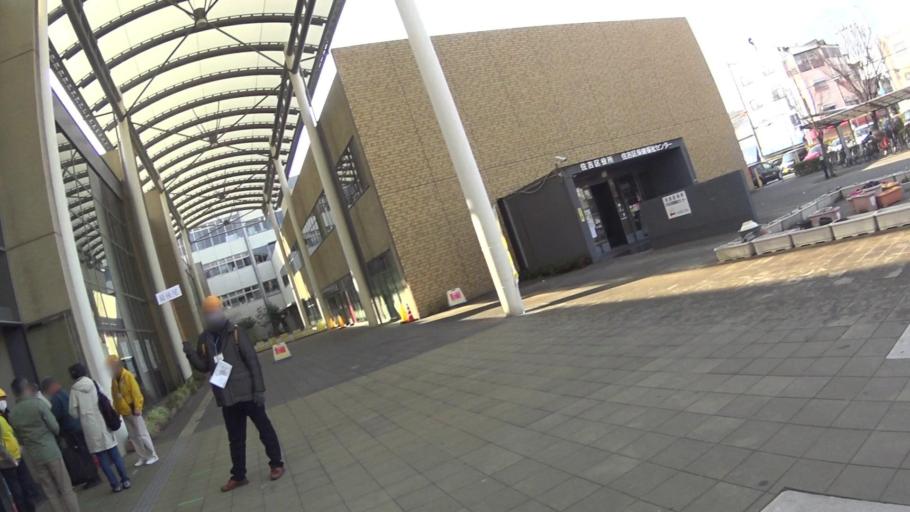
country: JP
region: Osaka
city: Sakai
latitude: 34.6044
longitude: 135.5006
